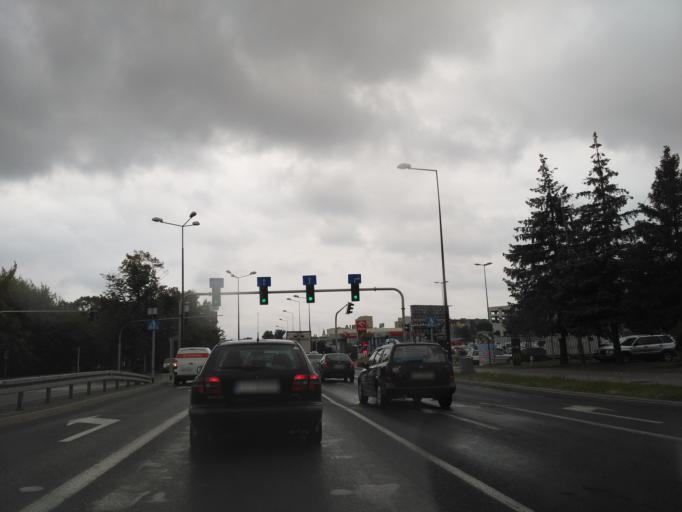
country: PL
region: Lublin Voivodeship
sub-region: Powiat lubelski
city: Lublin
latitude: 51.2658
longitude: 22.5727
